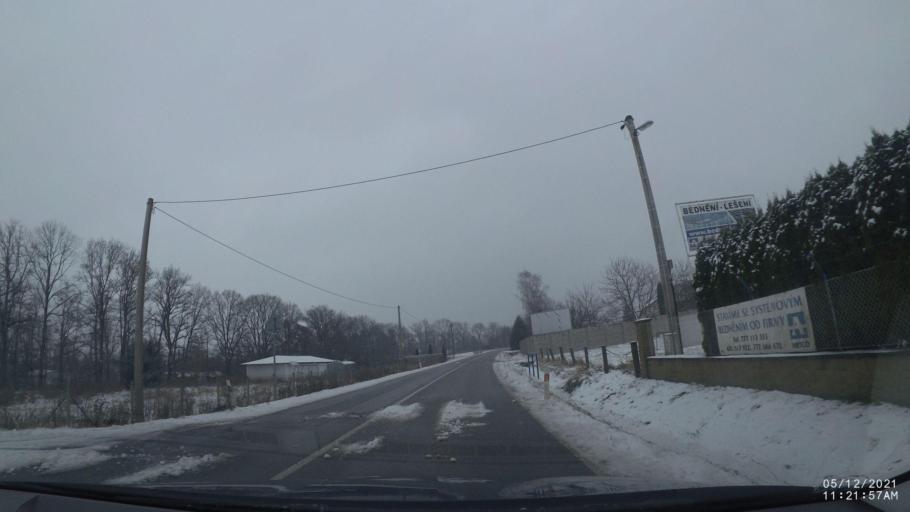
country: CZ
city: Solnice
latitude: 50.1942
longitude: 16.2299
